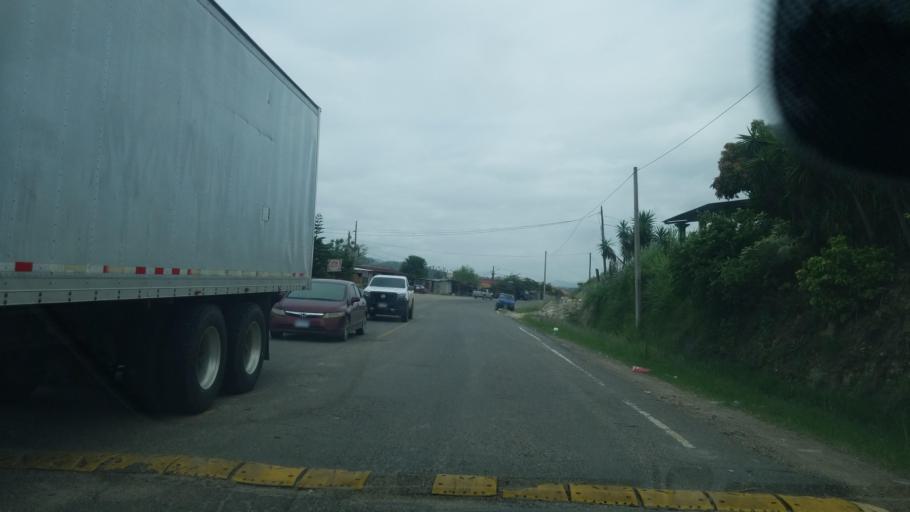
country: HN
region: Ocotepeque
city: Lucerna
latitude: 14.5579
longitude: -88.9395
